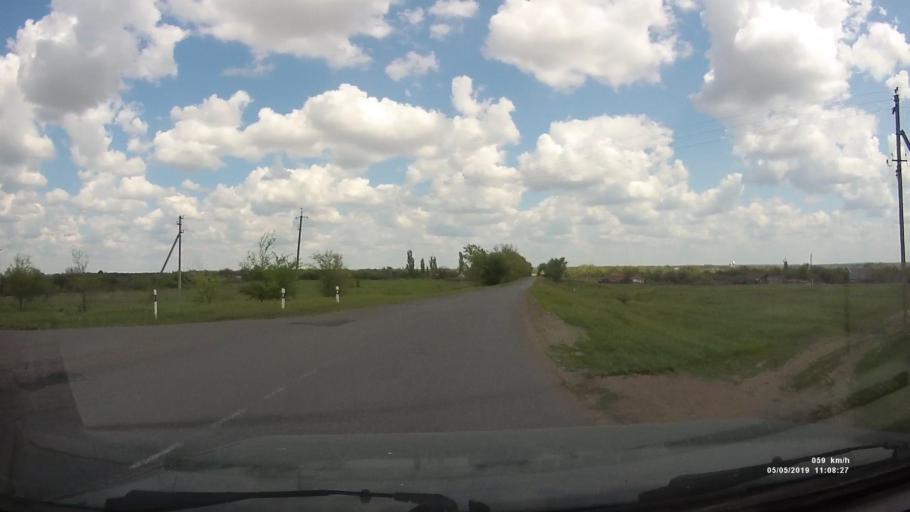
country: RU
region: Rostov
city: Ust'-Donetskiy
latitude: 47.7341
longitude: 40.9145
